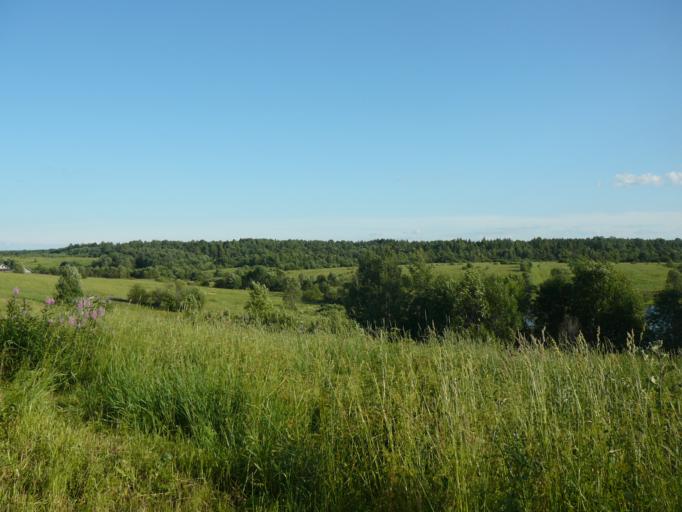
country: RU
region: Vologda
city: Vozhega
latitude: 60.3164
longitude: 39.5693
